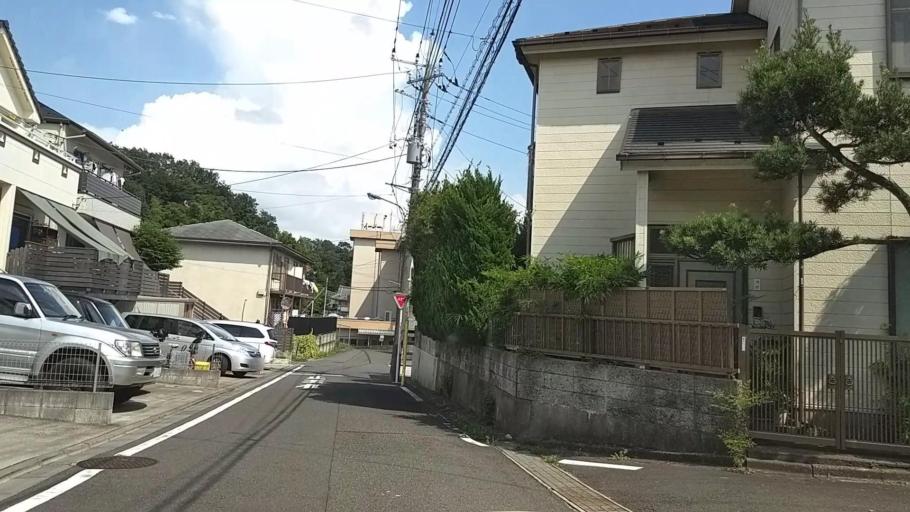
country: JP
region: Tokyo
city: Hachioji
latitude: 35.6473
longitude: 139.3123
